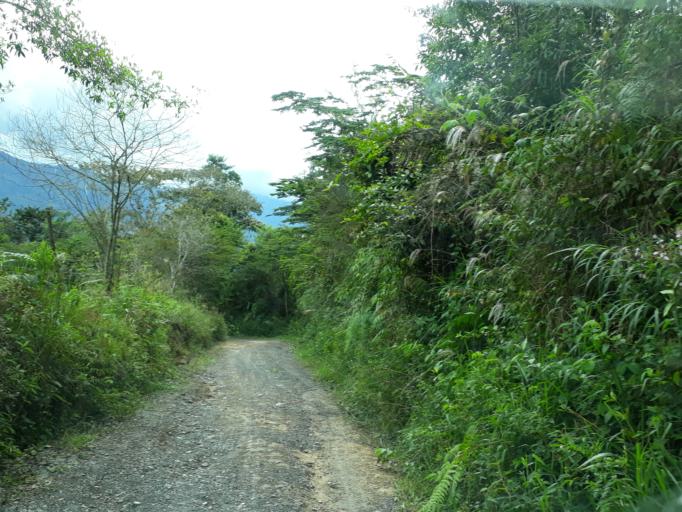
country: CO
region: Boyaca
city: Quipama
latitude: 5.3941
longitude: -74.1271
